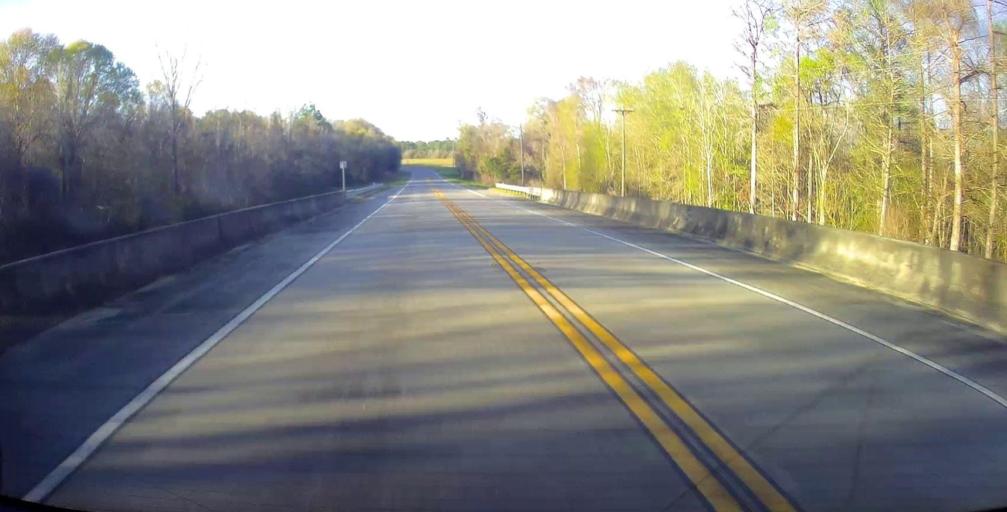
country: US
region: Georgia
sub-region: Pulaski County
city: Hawkinsville
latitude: 32.2495
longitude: -83.4104
